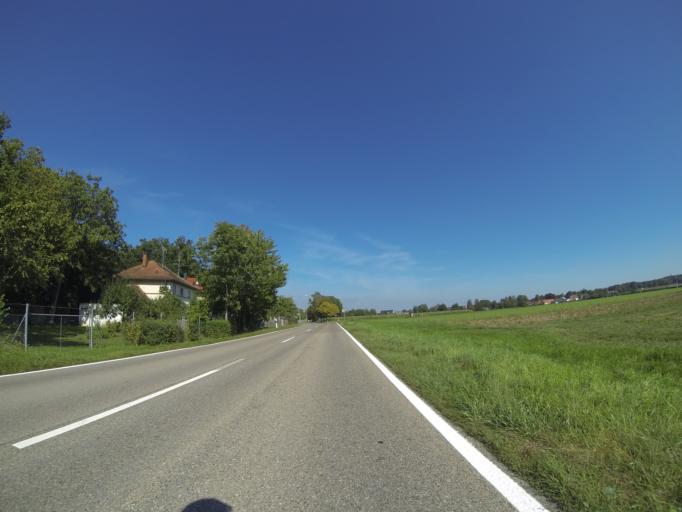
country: DE
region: Baden-Wuerttemberg
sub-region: Tuebingen Region
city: Erbach
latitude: 48.3230
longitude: 9.9248
